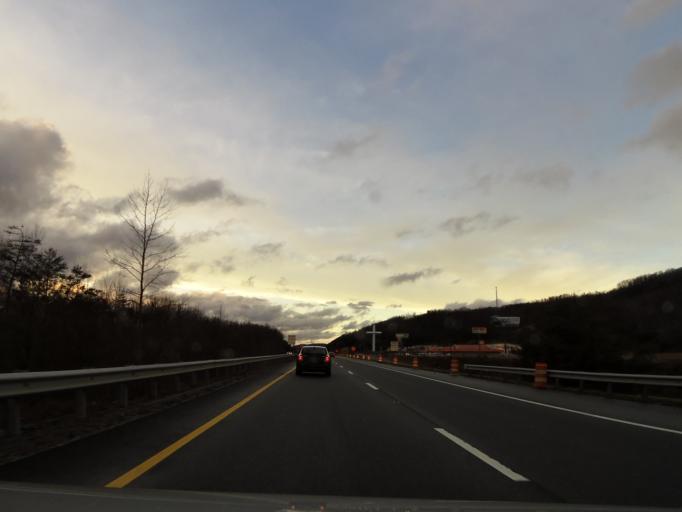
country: US
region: Tennessee
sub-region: Campbell County
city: Jacksboro
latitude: 36.3705
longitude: -84.2364
